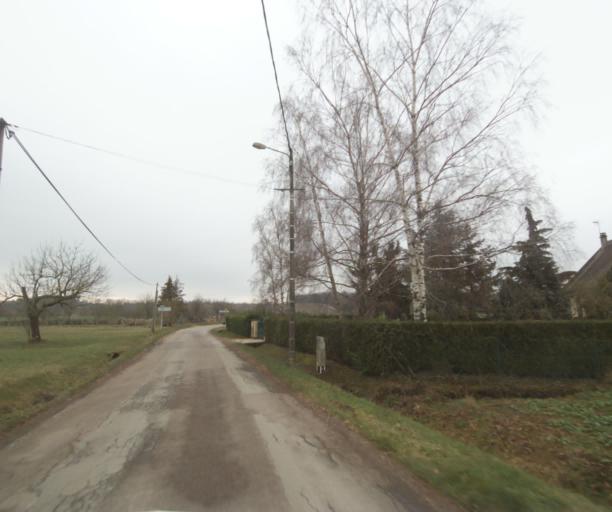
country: FR
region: Champagne-Ardenne
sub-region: Departement de la Haute-Marne
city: Wassy
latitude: 48.5406
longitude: 4.9813
